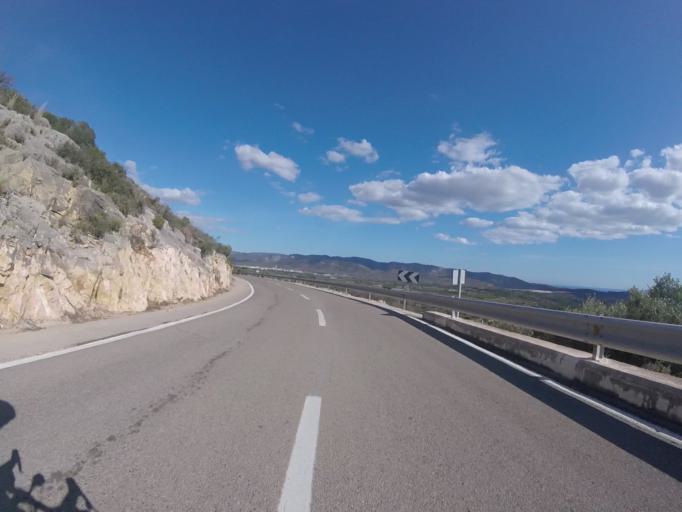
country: ES
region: Valencia
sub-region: Provincia de Castello
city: Alcala de Xivert
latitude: 40.2944
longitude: 0.1844
